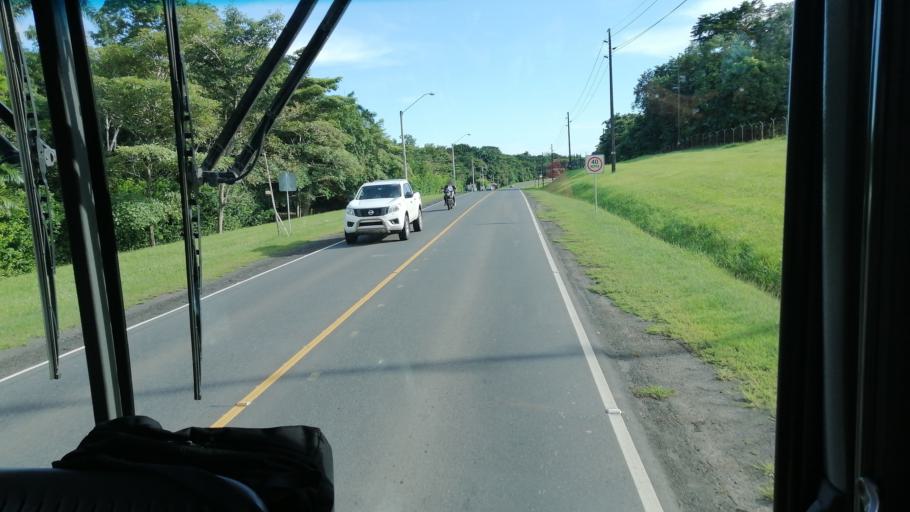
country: PA
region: Panama
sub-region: Distrito de Panama
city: Ancon
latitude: 8.9370
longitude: -79.5910
